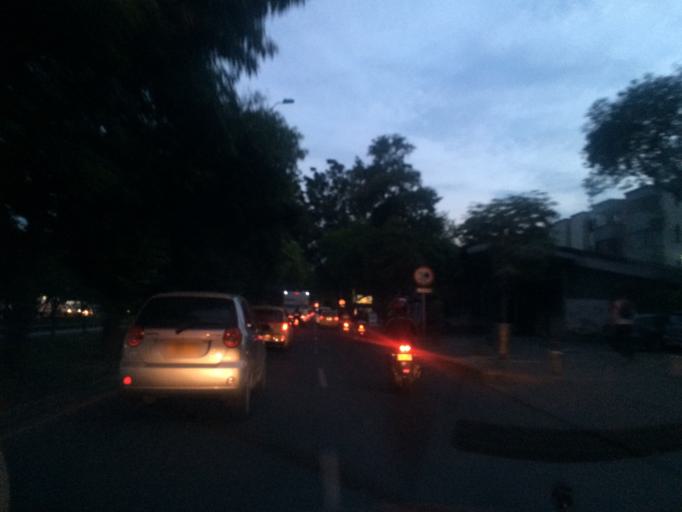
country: CO
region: Valle del Cauca
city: Cali
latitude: 3.4221
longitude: -76.5476
